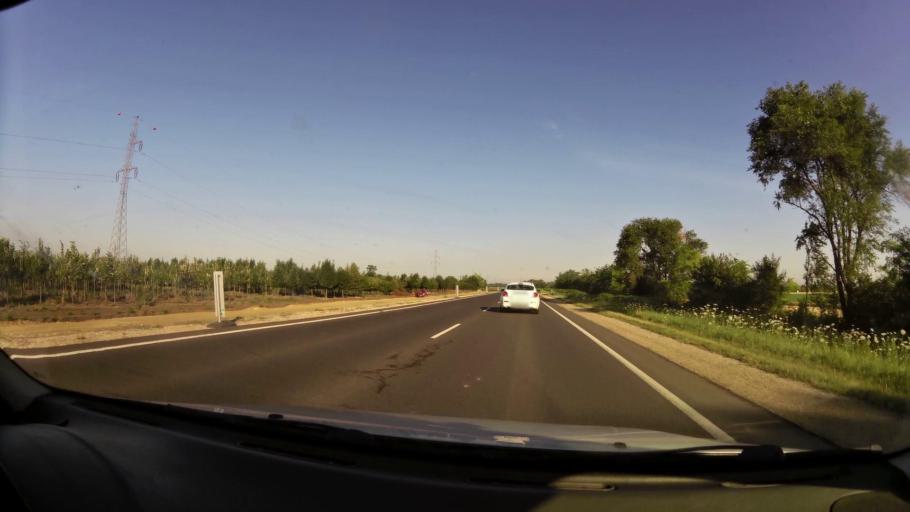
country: HU
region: Pest
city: Cegledbercel
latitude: 47.2149
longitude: 19.7287
